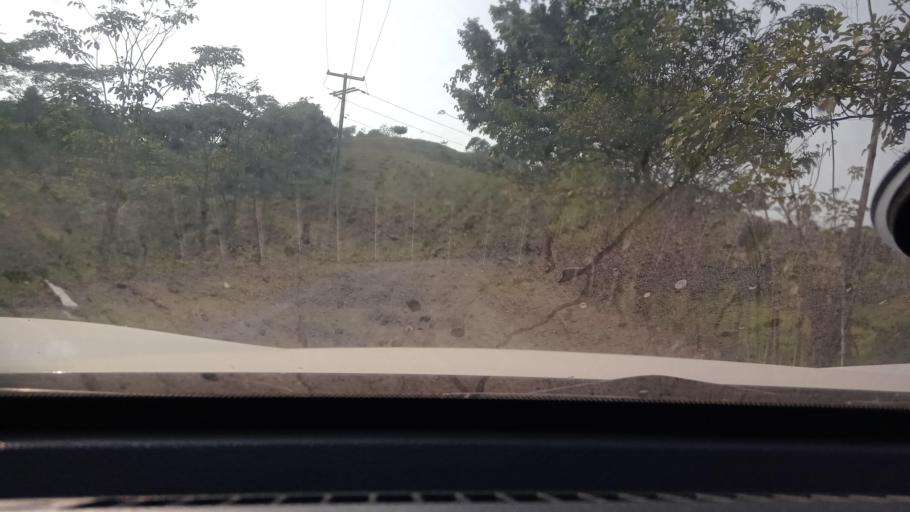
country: MX
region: Tabasco
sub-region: Huimanguillo
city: Francisco Rueda
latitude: 17.6610
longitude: -93.8616
